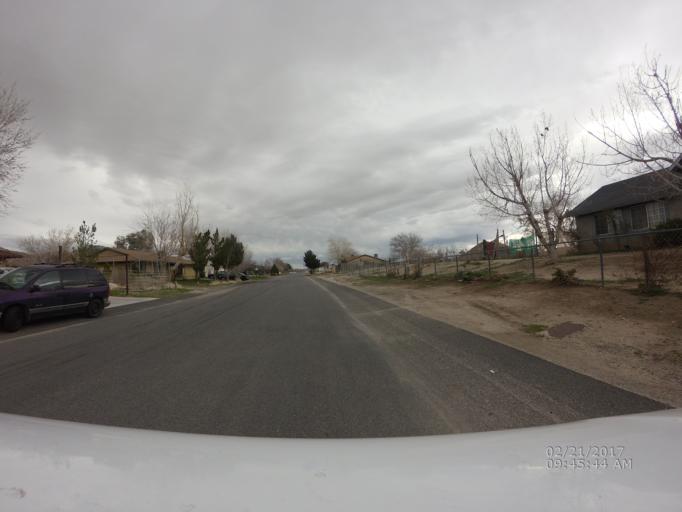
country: US
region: California
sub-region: Los Angeles County
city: Lake Los Angeles
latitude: 34.5986
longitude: -117.8219
